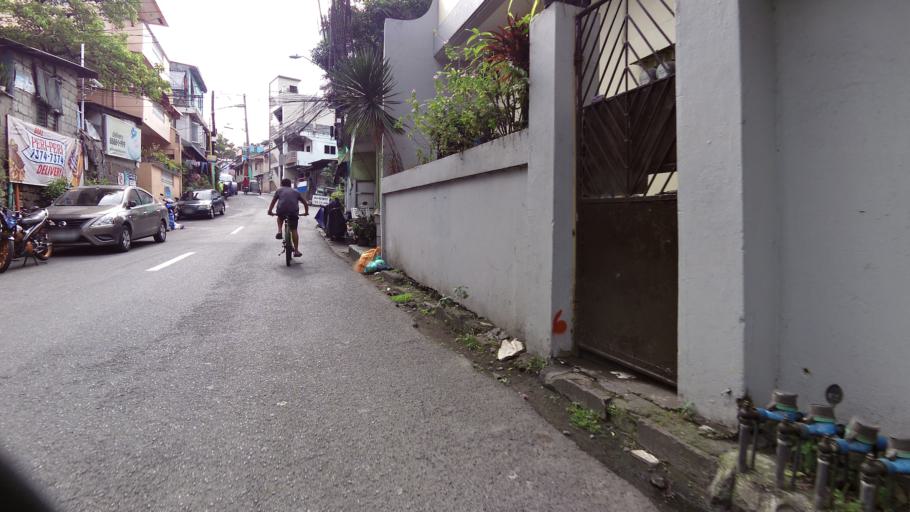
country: PH
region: Metro Manila
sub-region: Pasig
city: Pasig City
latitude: 14.5645
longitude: 121.0621
